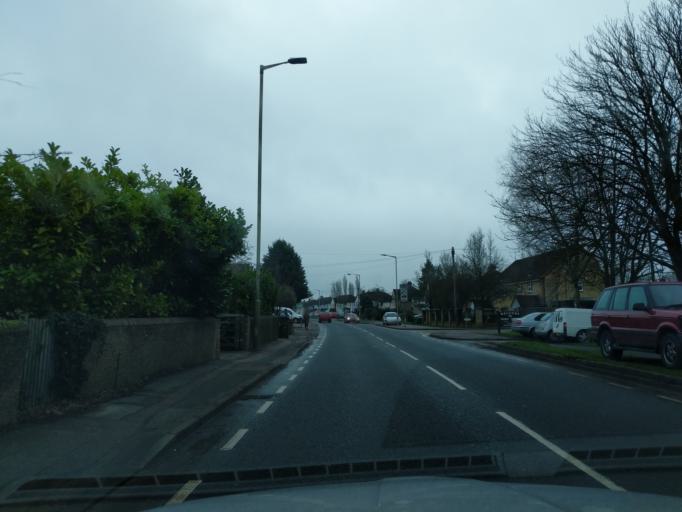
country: GB
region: England
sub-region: Hertfordshire
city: Kings Langley
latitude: 51.7336
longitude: -0.4572
